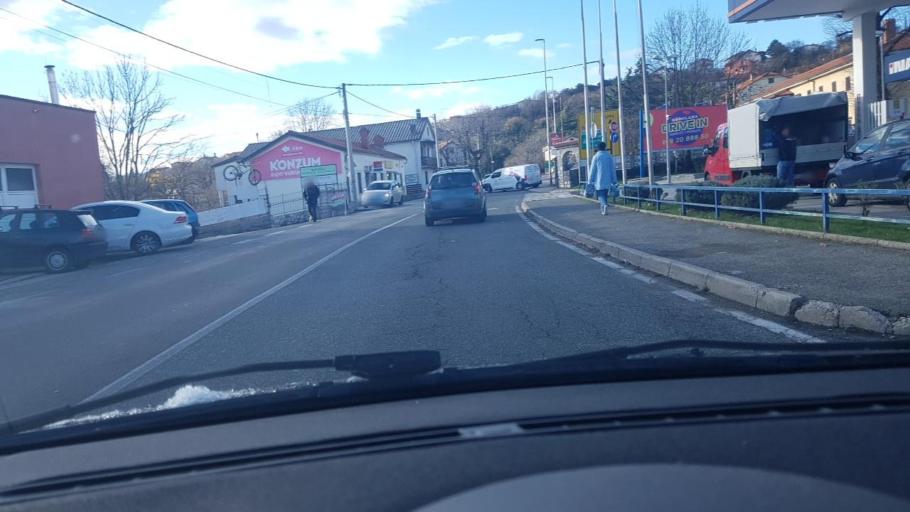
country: HR
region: Primorsko-Goranska
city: Cavle
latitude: 45.3565
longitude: 14.4878
